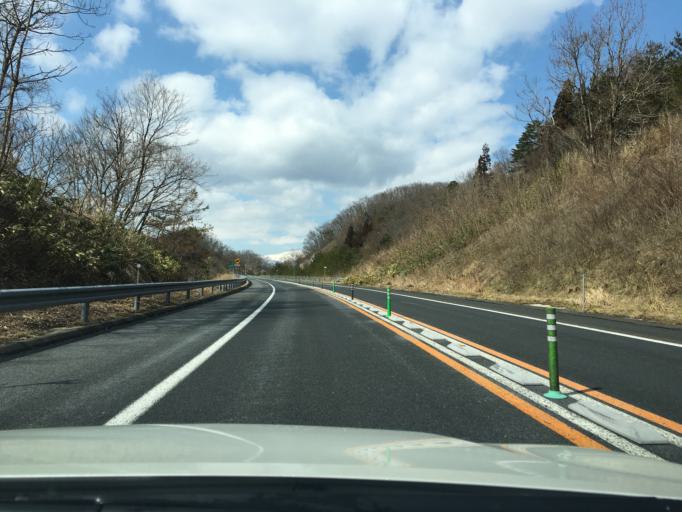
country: JP
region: Yamagata
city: Sagae
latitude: 38.3889
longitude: 140.2197
